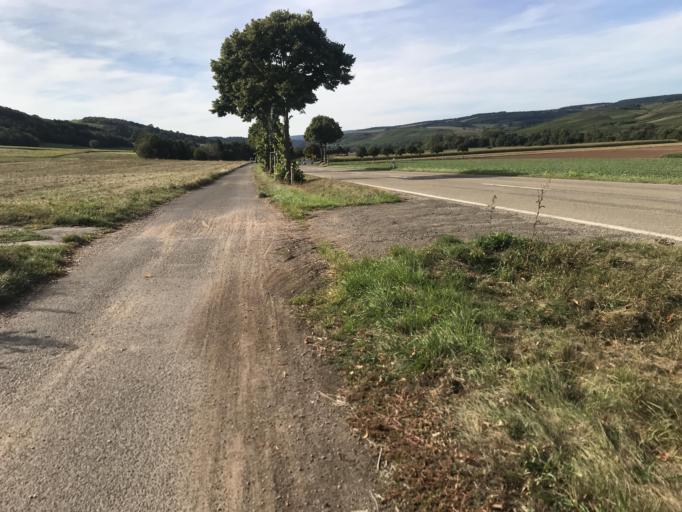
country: DE
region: Rheinland-Pfalz
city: Monzingen
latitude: 49.7872
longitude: 7.5851
